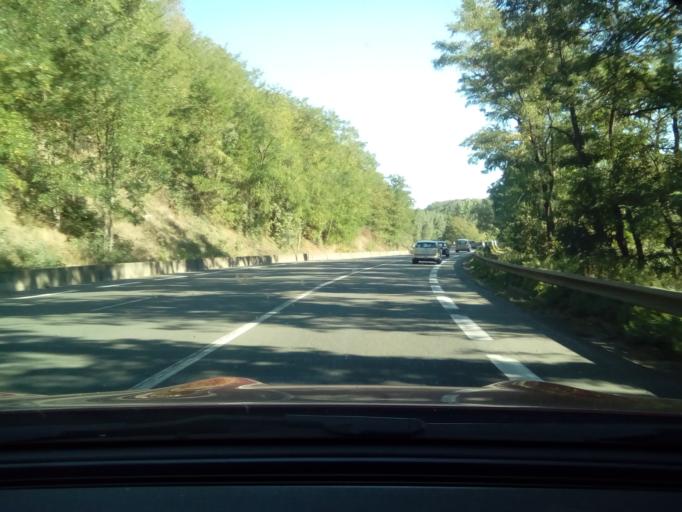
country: FR
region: Rhone-Alpes
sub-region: Departement du Rhone
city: Charnay
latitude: 45.8675
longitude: 4.6603
